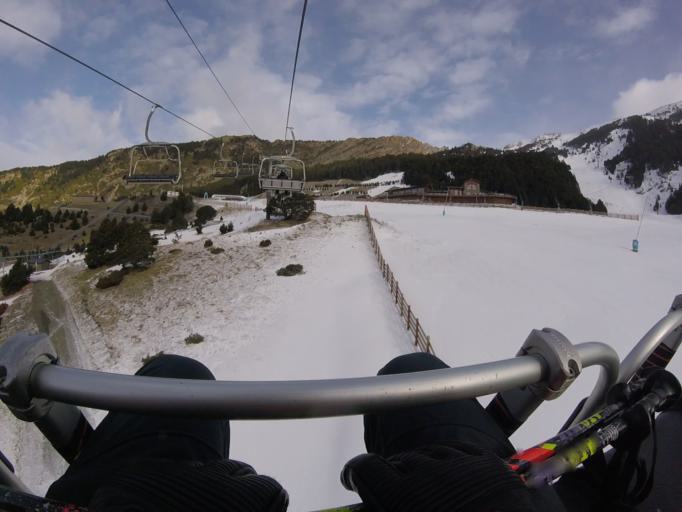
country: AD
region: Canillo
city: Canillo
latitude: 42.5544
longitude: 1.6143
